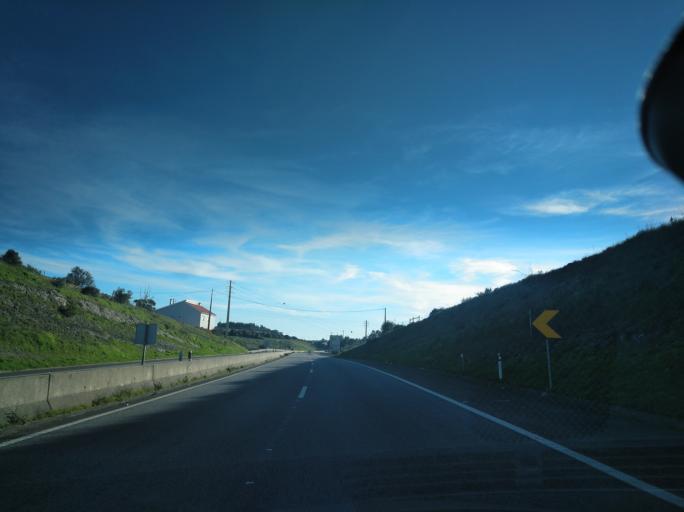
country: PT
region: Lisbon
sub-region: Sintra
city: Pero Pinheiro
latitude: 38.8521
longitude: -9.3497
